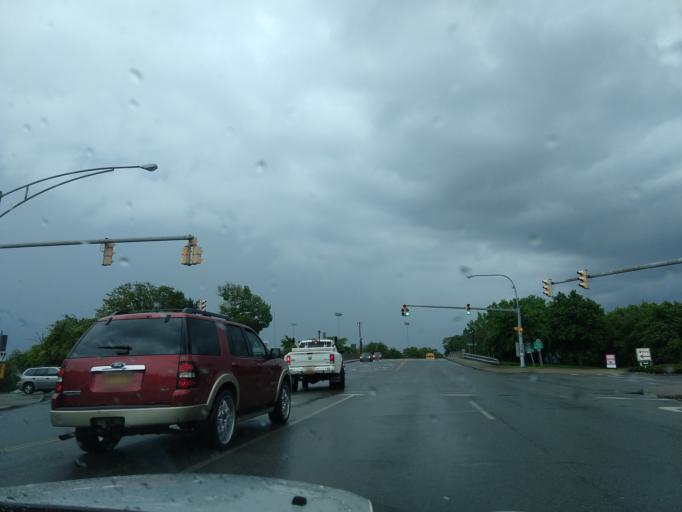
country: US
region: New York
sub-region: Erie County
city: Kenmore
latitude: 42.9377
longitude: -78.8896
